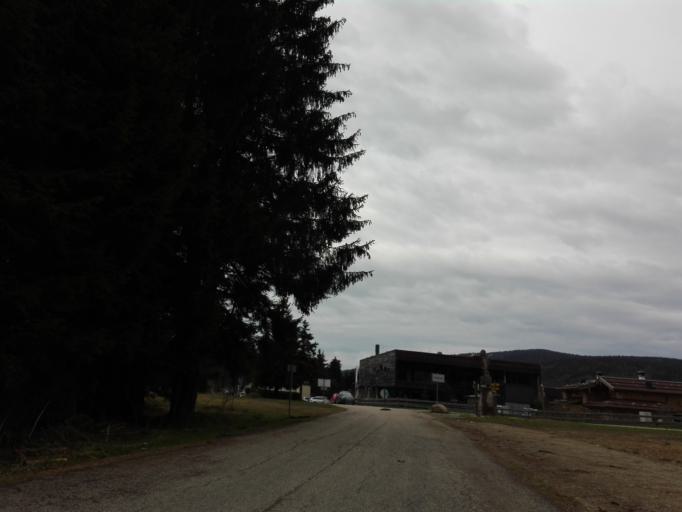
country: AT
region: Upper Austria
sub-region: Politischer Bezirk Rohrbach
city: Ulrichsberg
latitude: 48.7044
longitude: 13.9484
